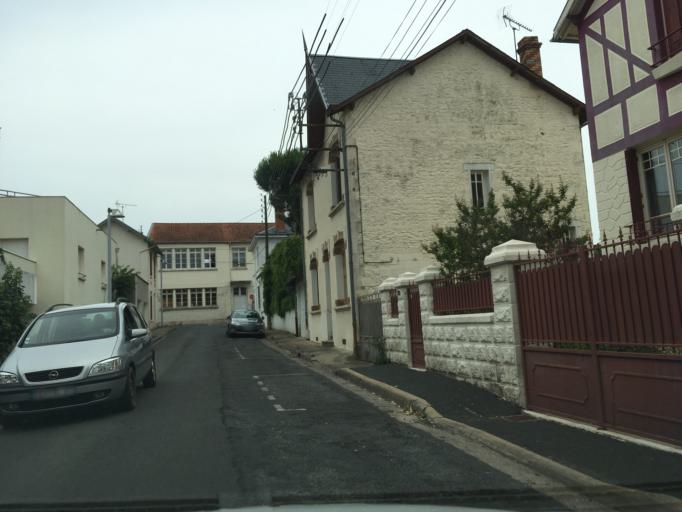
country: FR
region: Poitou-Charentes
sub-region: Departement des Deux-Sevres
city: Niort
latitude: 46.3267
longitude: -0.4689
